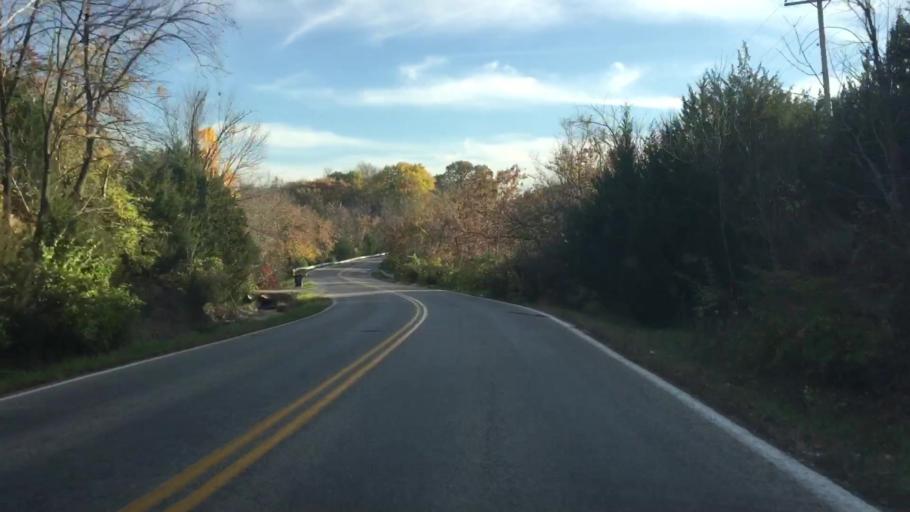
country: US
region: Kansas
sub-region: Wyandotte County
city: Edwardsville
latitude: 39.0194
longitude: -94.7800
